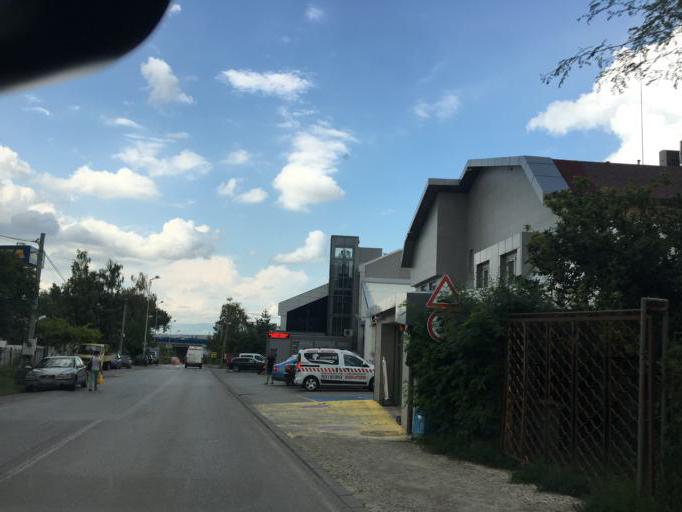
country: BG
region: Sofia-Capital
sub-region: Stolichna Obshtina
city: Sofia
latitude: 42.6217
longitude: 23.3585
